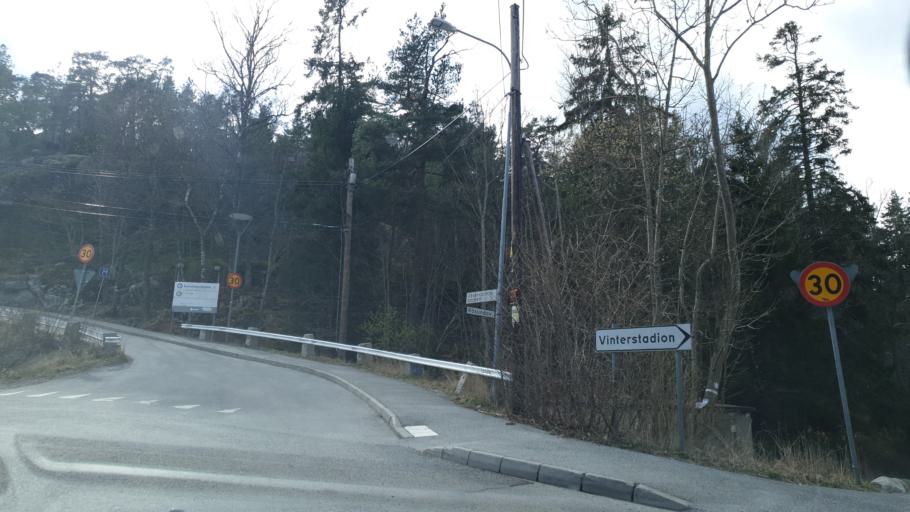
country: SE
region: Stockholm
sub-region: Nacka Kommun
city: Saltsjobaden
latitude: 59.2732
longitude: 18.3060
